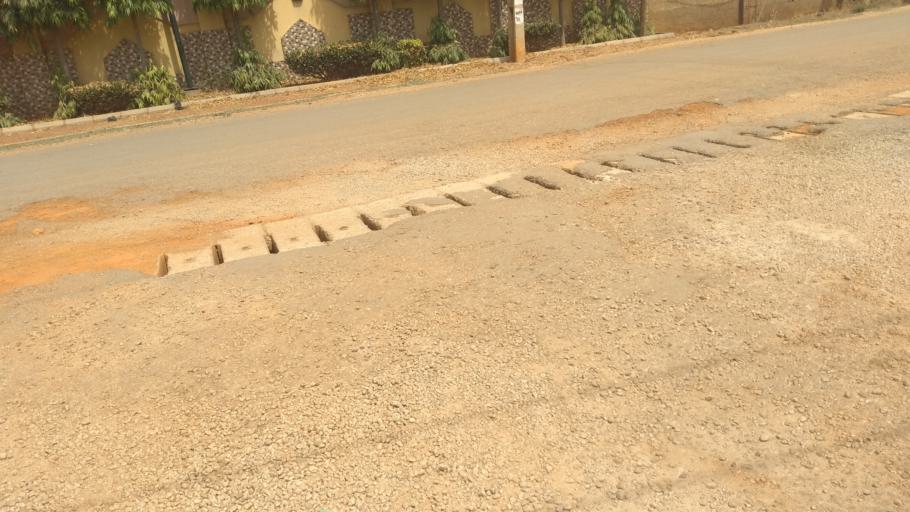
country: NG
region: Kaduna
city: Kaduna
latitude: 10.5786
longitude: 7.4264
